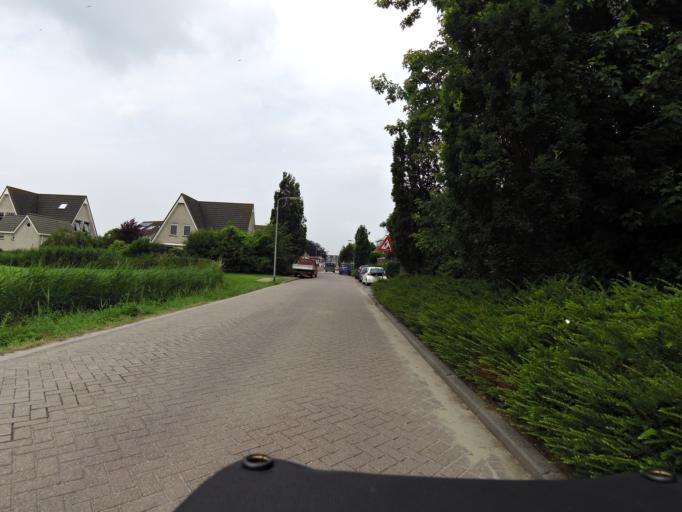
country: NL
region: South Holland
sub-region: Gemeente Hellevoetsluis
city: Nieuwenhoorn
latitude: 51.8523
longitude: 4.1446
